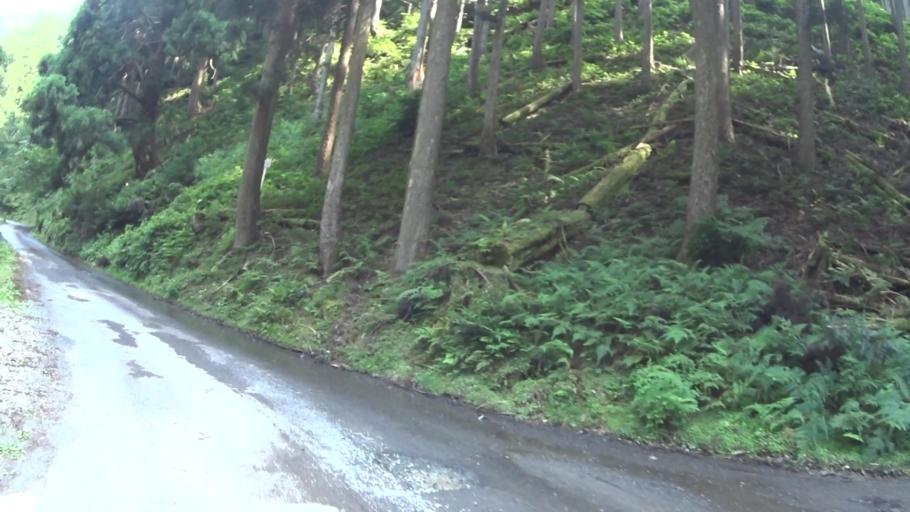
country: JP
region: Fukui
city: Obama
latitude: 35.2735
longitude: 135.6395
